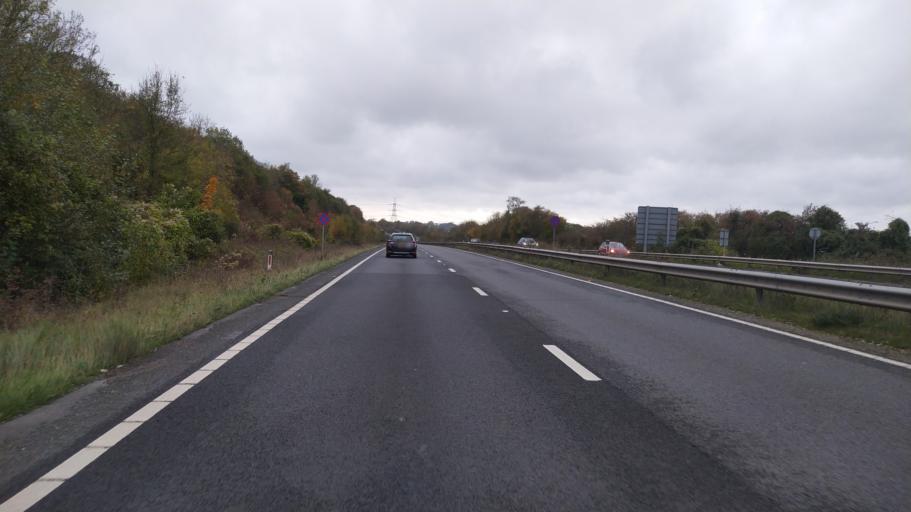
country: GB
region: England
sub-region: Hampshire
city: Cowplain
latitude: 50.9403
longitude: -0.9884
